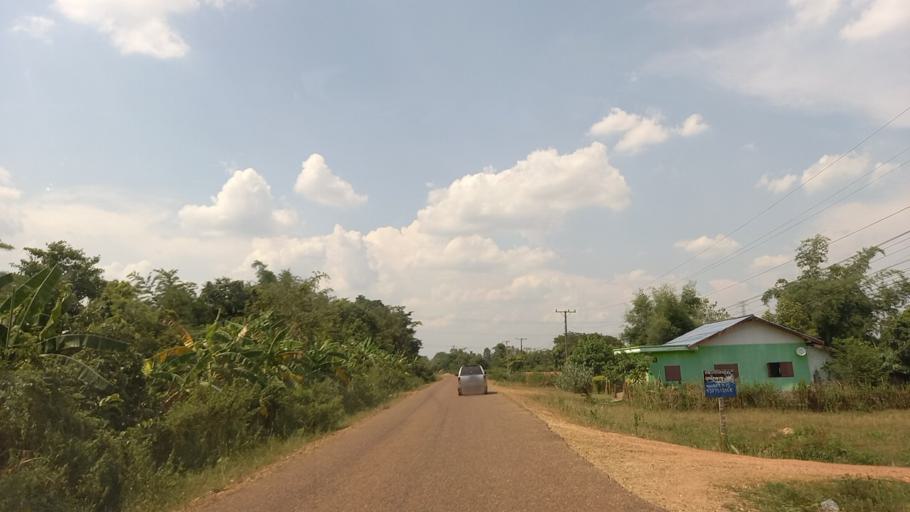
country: LA
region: Bolikhamxai
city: Muang Pakxan
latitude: 18.4095
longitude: 103.7024
